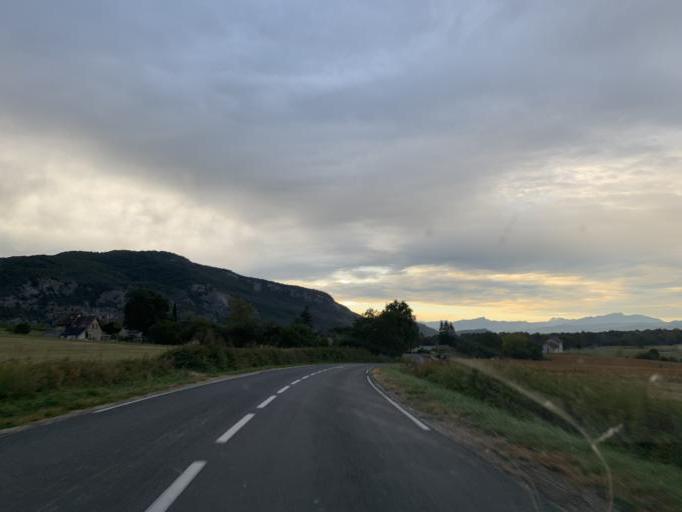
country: FR
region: Rhone-Alpes
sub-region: Departement de l'Isere
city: Les Avenieres
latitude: 45.7070
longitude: 5.5734
